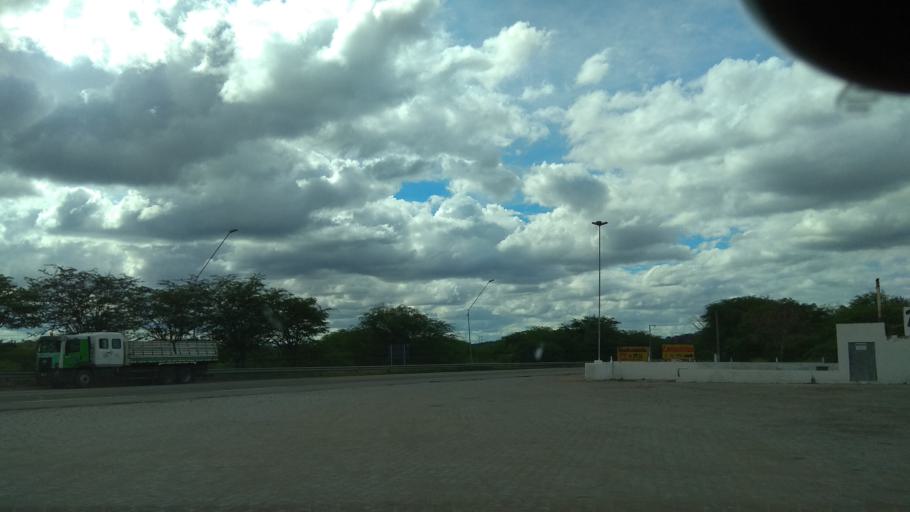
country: BR
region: Bahia
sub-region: Santa Ines
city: Santa Ines
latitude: -12.9824
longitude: -39.9413
